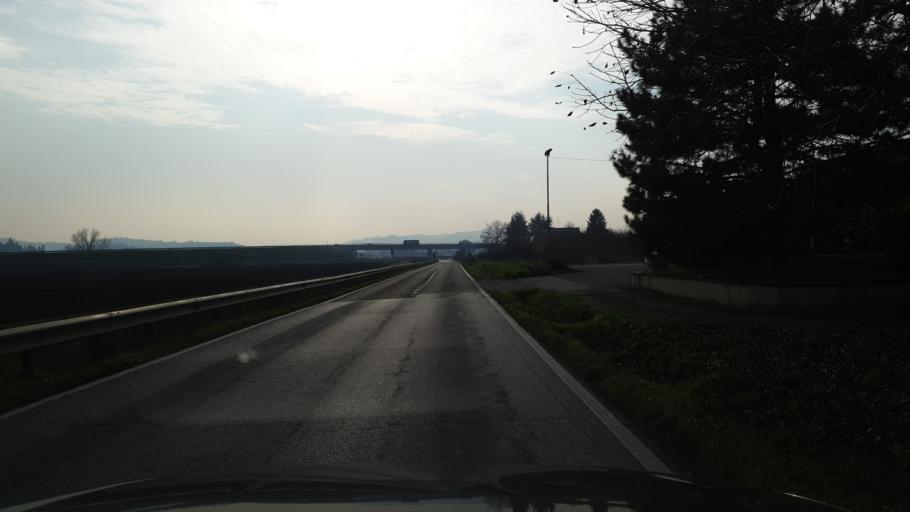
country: IT
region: Emilia-Romagna
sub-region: Provincia di Bologna
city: Crespellano
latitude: 44.5199
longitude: 11.1159
